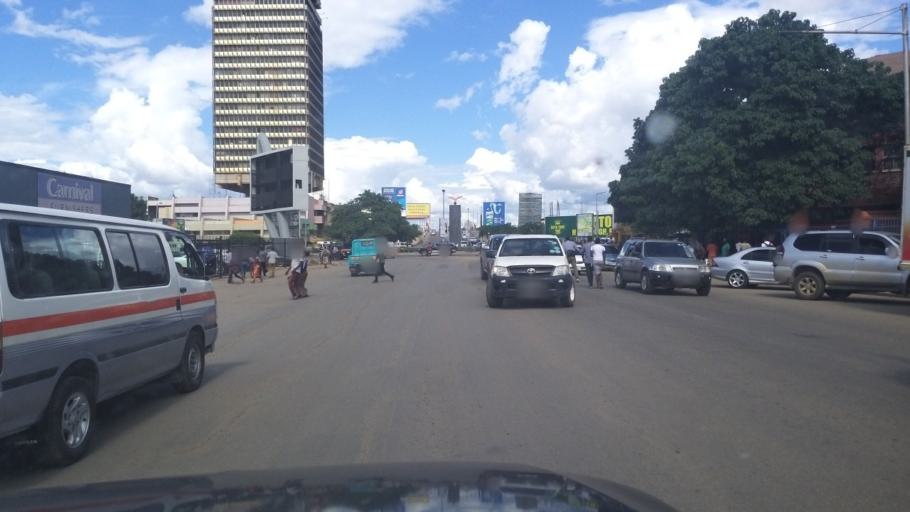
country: ZM
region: Lusaka
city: Lusaka
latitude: -15.4251
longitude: 28.2820
